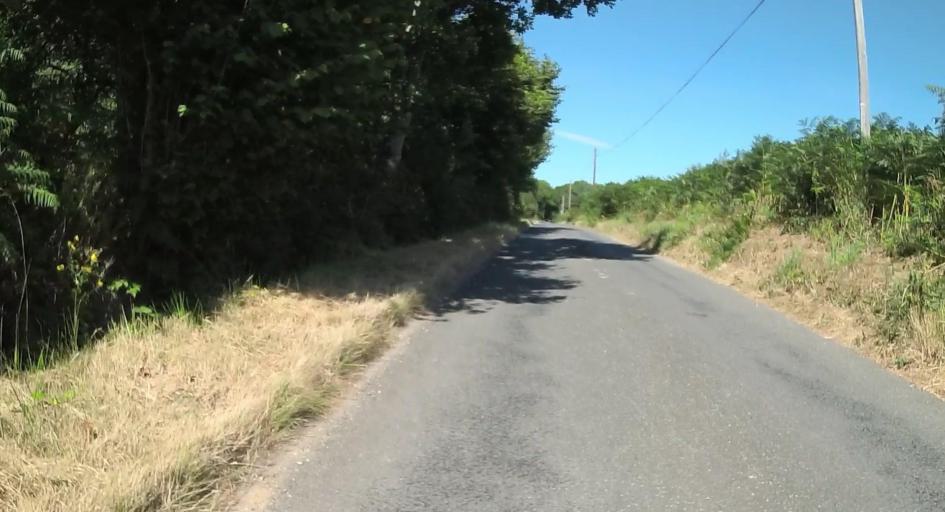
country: GB
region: England
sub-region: Dorset
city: Bovington Camp
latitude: 50.7402
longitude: -2.2238
